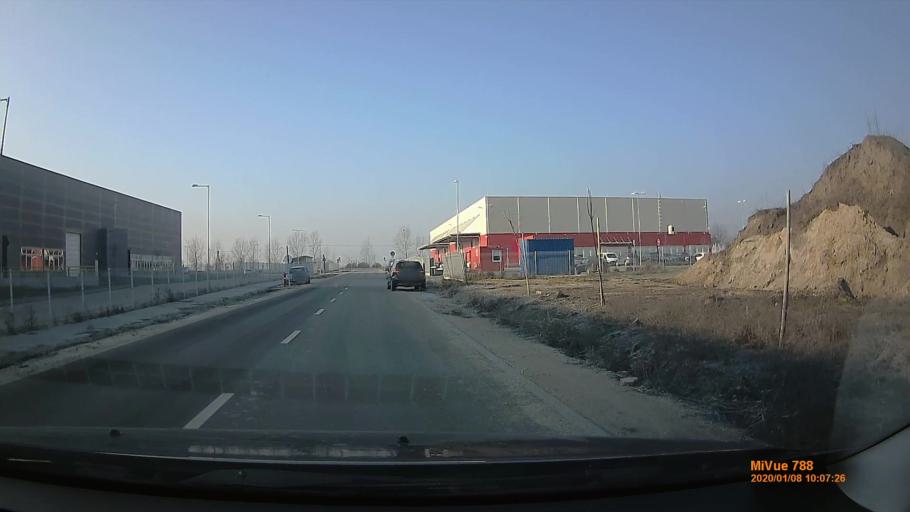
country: HU
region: Bacs-Kiskun
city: Kecskemet
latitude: 46.8749
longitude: 19.7026
